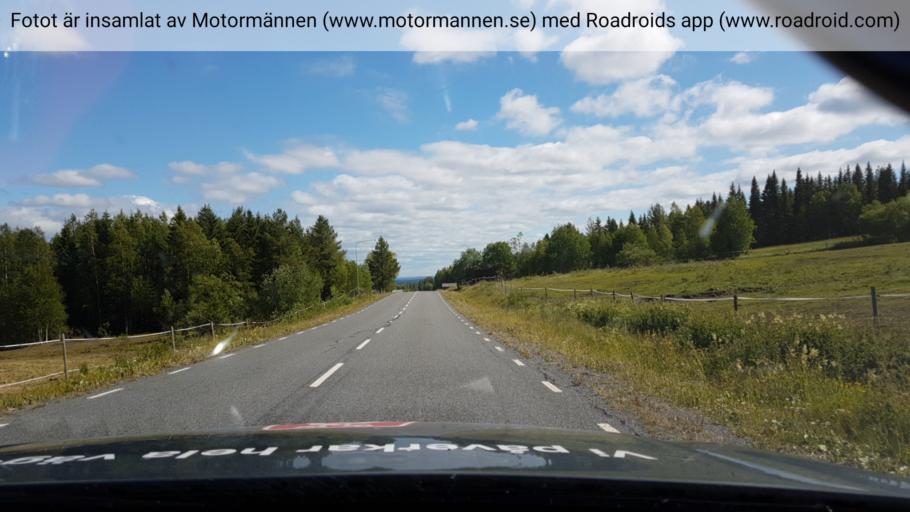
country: SE
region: Jaemtland
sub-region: OEstersunds Kommun
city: Lit
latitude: 63.3669
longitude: 15.1963
